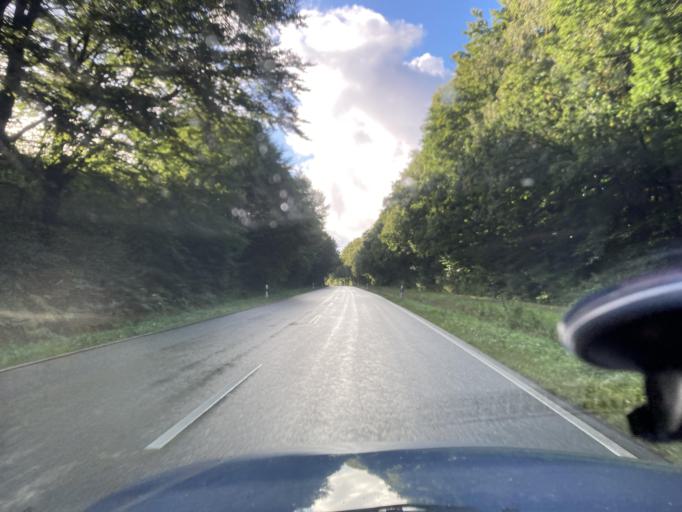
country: DE
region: Schleswig-Holstein
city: Nordhastedt
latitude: 54.1957
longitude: 9.1790
